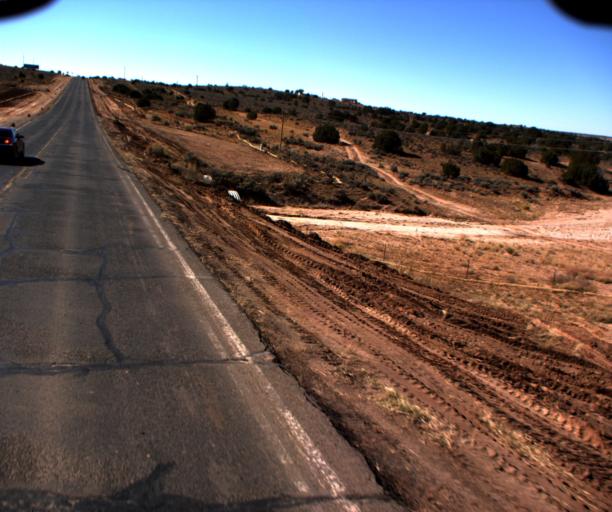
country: US
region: Arizona
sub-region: Apache County
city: Ganado
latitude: 35.7117
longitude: -109.4978
